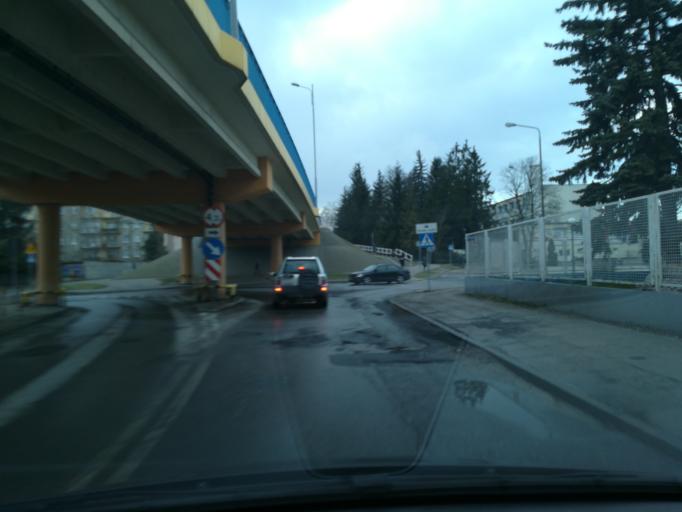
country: PL
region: Lodz Voivodeship
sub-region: Powiat radomszczanski
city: Radomsko
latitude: 51.0695
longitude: 19.4345
